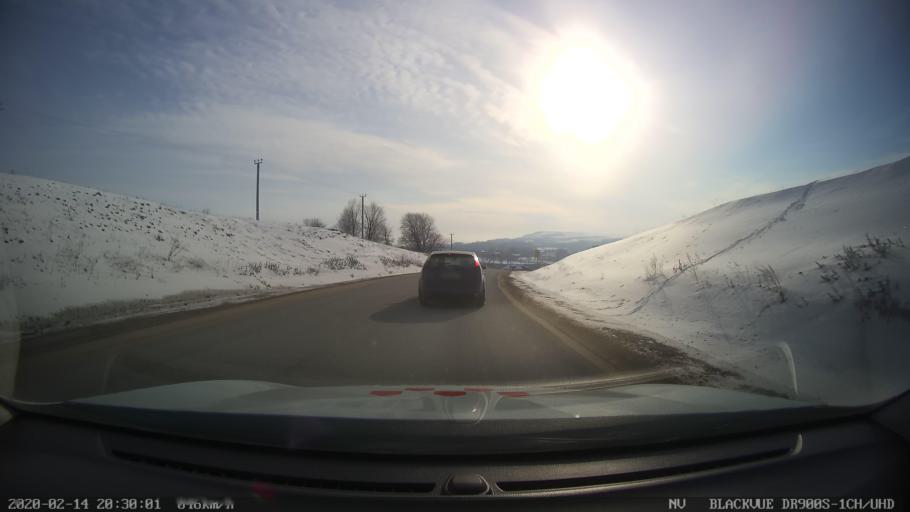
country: RU
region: Tatarstan
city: Stolbishchi
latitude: 55.4455
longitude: 48.9931
